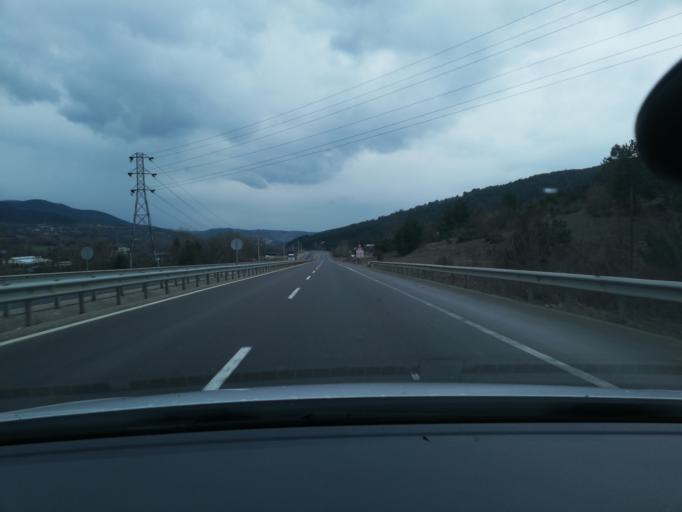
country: TR
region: Bolu
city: Yenicaga
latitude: 40.7455
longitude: 31.8653
